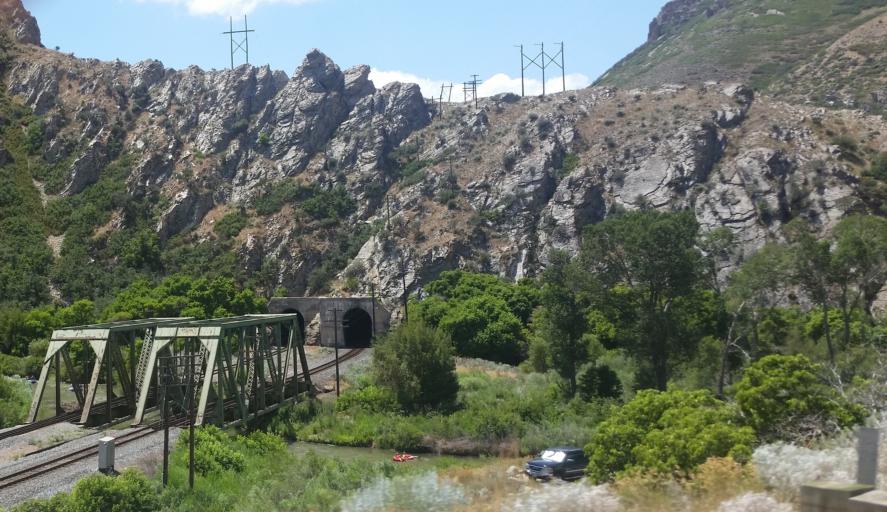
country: US
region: Utah
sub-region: Morgan County
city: Morgan
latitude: 41.0595
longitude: -111.5868
